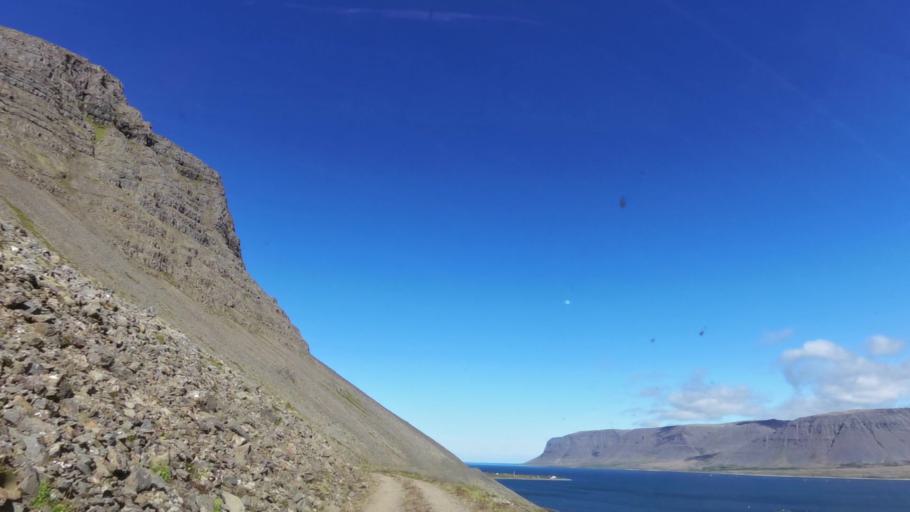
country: IS
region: West
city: Olafsvik
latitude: 65.6293
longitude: -23.9092
